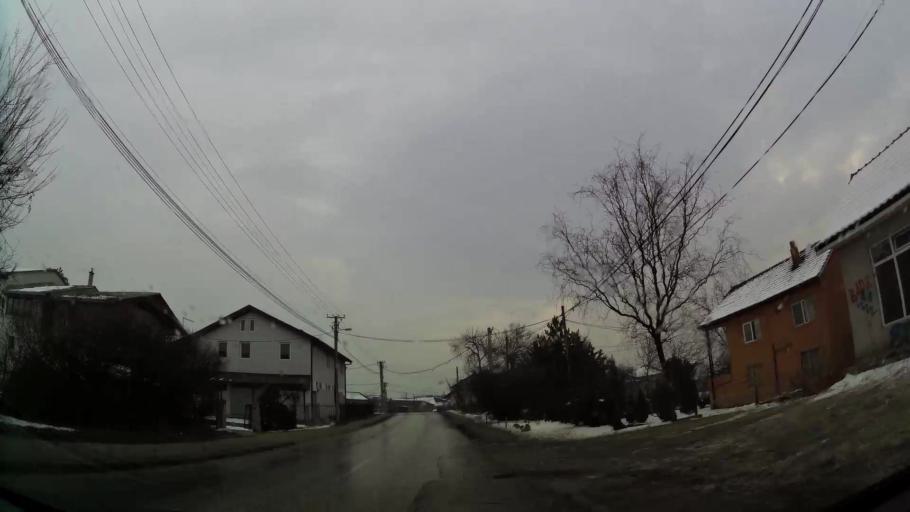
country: MK
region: Saraj
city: Saraj
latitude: 42.0300
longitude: 21.3513
